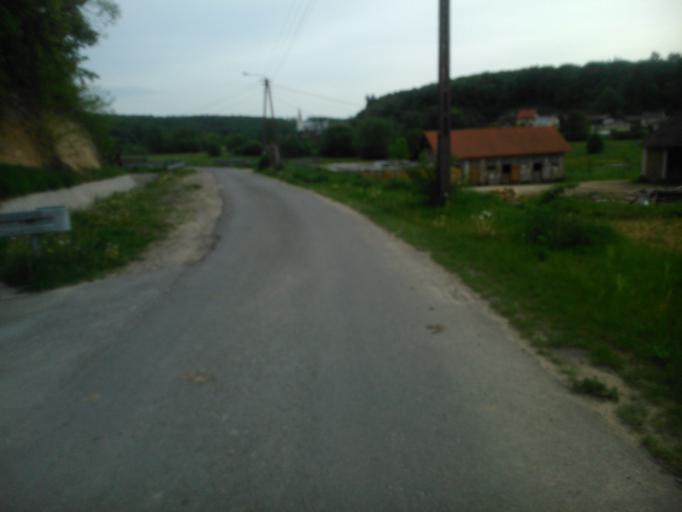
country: PL
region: Swietokrzyskie
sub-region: Powiat ostrowiecki
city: Baltow
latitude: 51.0139
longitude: 21.5418
